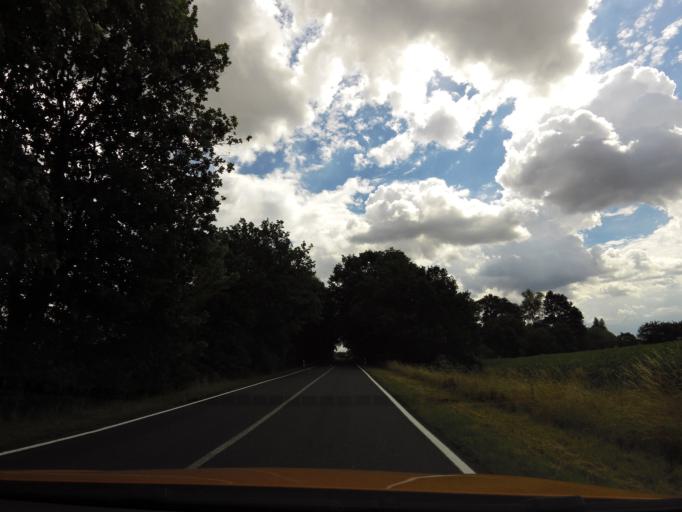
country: DE
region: Brandenburg
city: Rangsdorf
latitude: 52.3132
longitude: 13.4679
